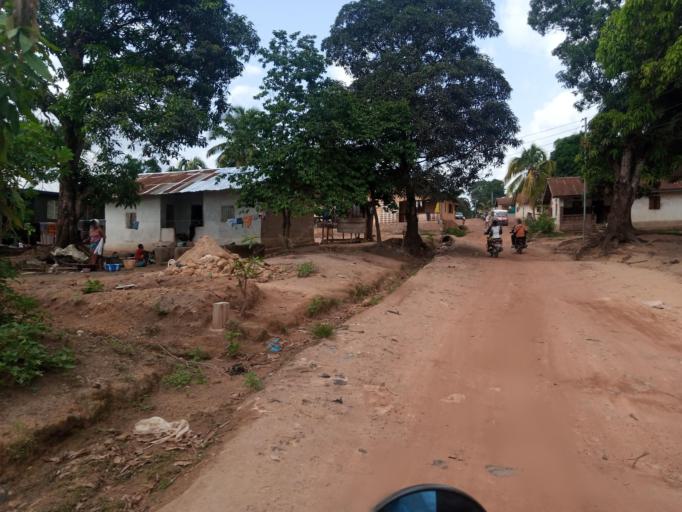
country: SL
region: Southern Province
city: Bo
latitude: 7.9818
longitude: -11.7320
